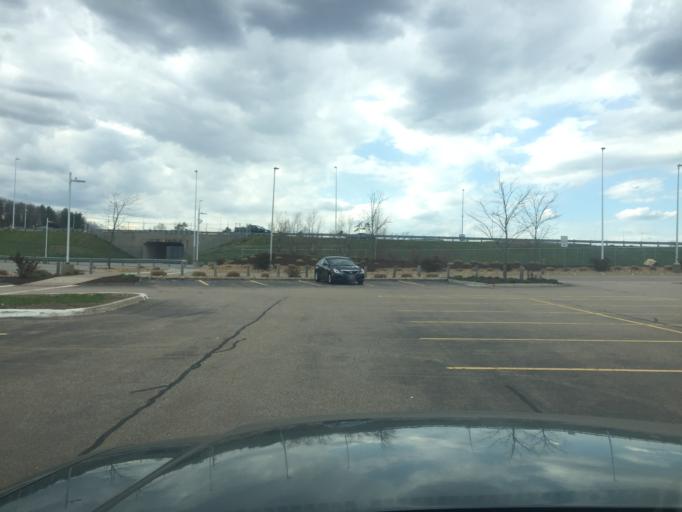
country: US
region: Massachusetts
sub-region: Norfolk County
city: Foxborough
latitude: 42.0878
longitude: -71.2689
